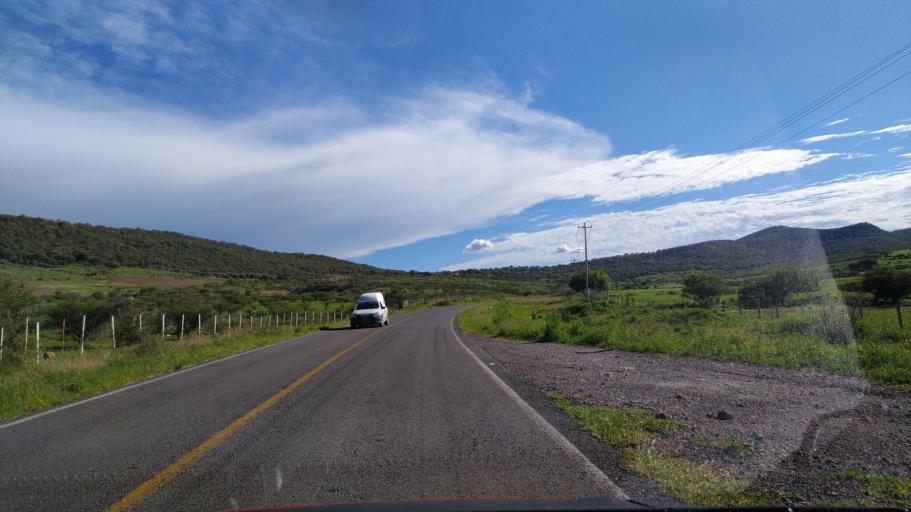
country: MX
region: Guanajuato
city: Ciudad Manuel Doblado
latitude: 20.6347
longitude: -101.9738
